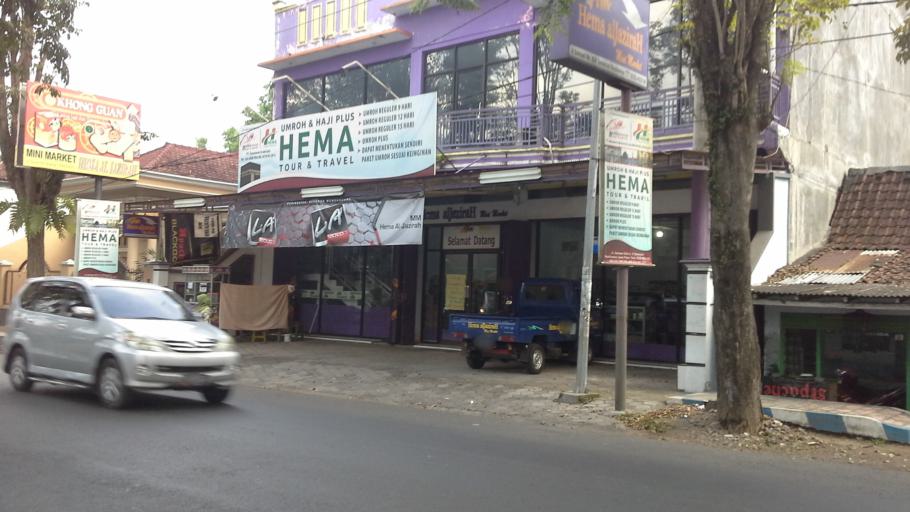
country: ID
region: East Java
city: Bondowoso
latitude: -7.9308
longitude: 113.8231
